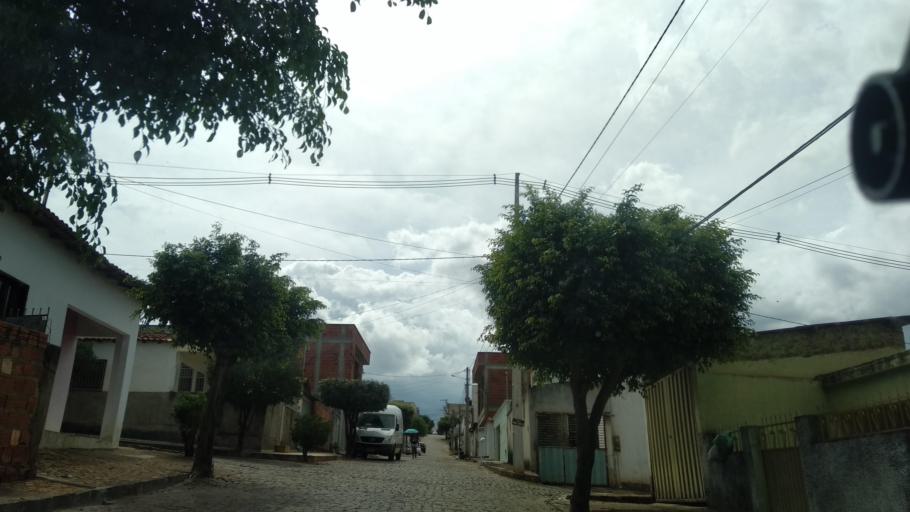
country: BR
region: Bahia
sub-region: Caetite
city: Caetite
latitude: -14.0636
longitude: -42.4799
